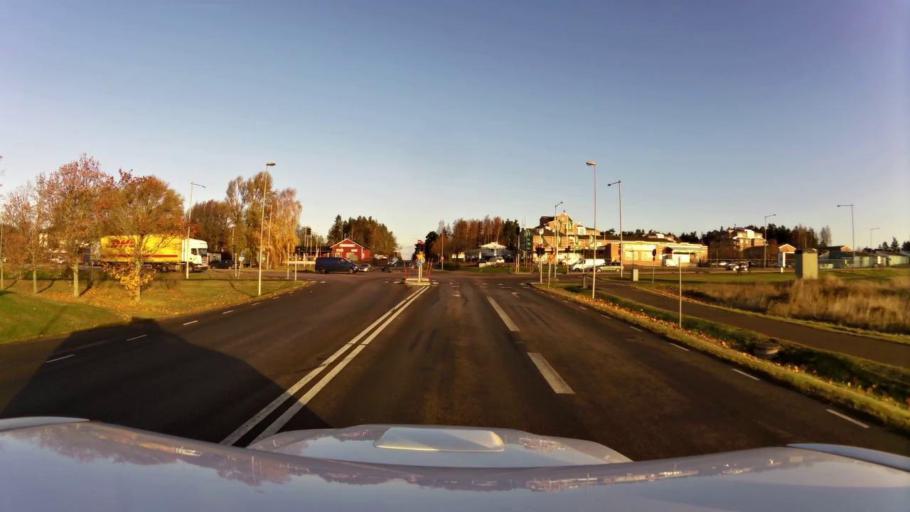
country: SE
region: OEstergoetland
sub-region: Linkopings Kommun
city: Linkoping
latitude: 58.4252
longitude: 15.6781
